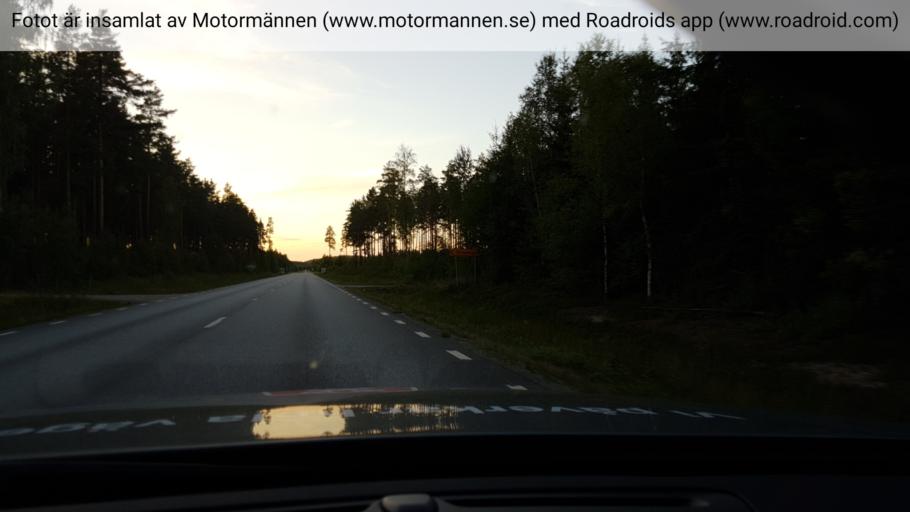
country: SE
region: OErebro
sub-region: Karlskoga Kommun
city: Karlskoga
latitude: 59.4192
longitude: 14.5165
